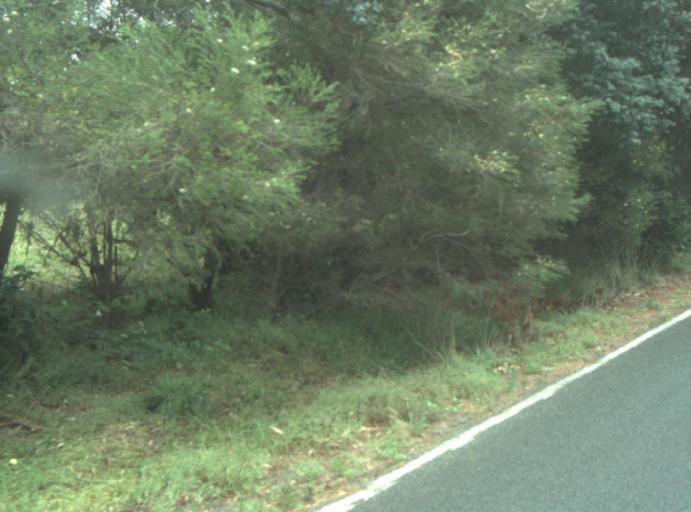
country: AU
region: Victoria
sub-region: Greater Geelong
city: Leopold
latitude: -38.2248
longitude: 144.5045
